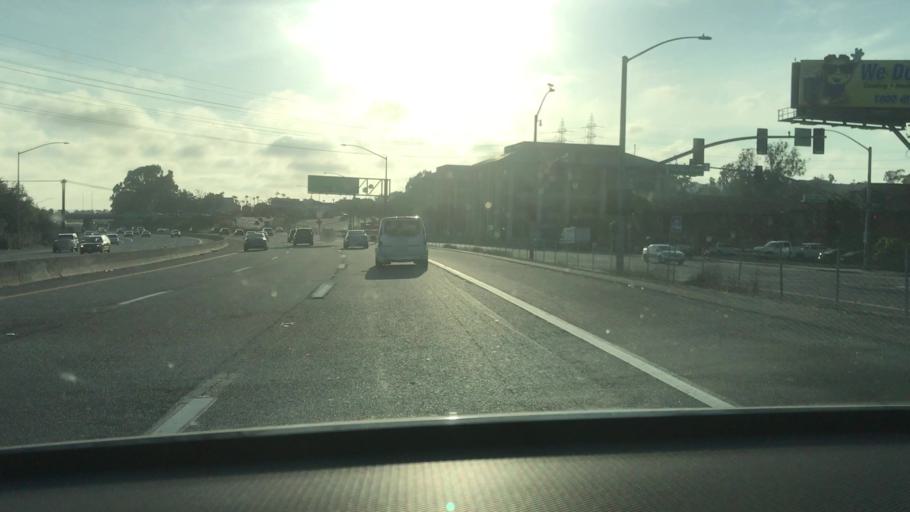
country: US
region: California
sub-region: San Diego County
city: Carlsbad
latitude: 33.1837
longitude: -117.3231
